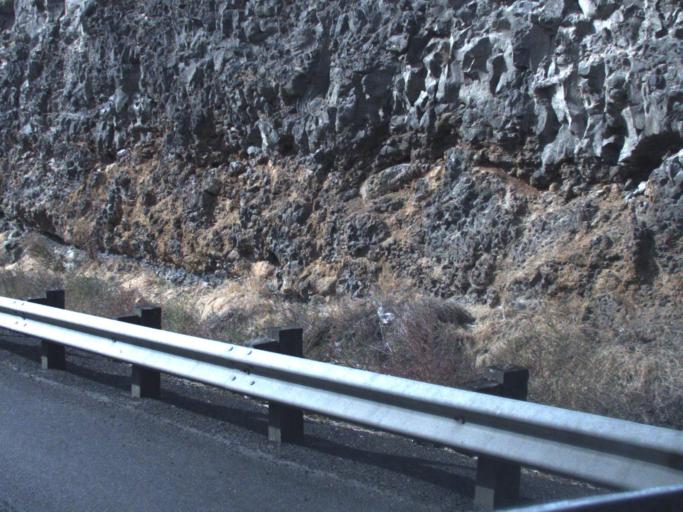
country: US
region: Washington
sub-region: Franklin County
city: Basin City
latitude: 46.5954
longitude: -119.0064
